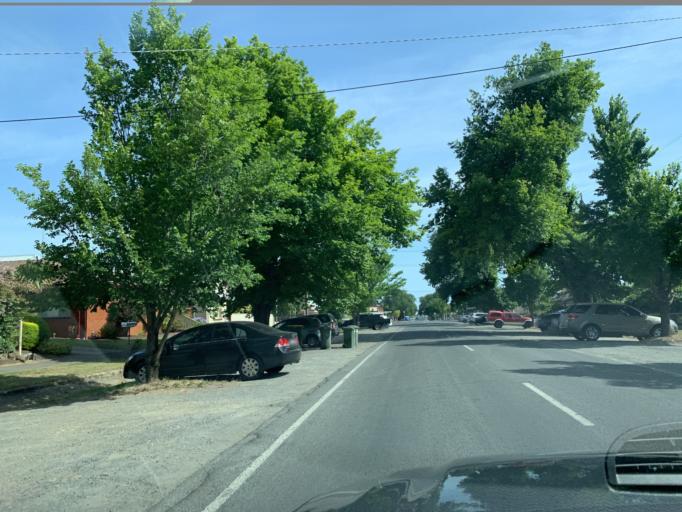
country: AU
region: Victoria
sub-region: Ballarat North
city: Ballarat Central
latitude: -37.5587
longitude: 143.8448
